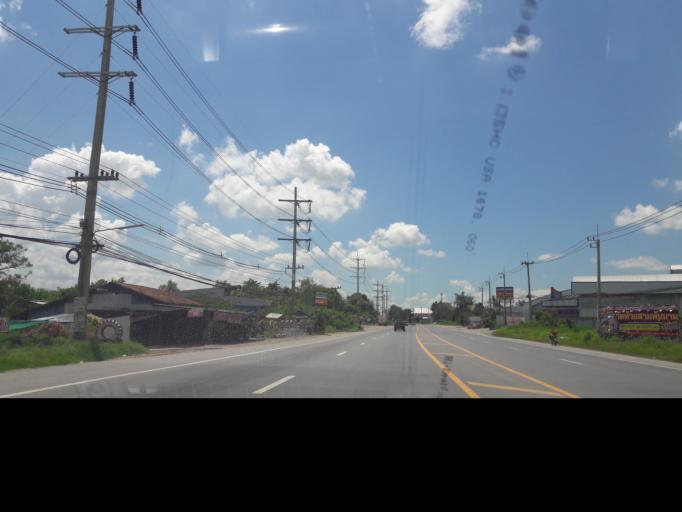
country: TH
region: Nakhon Pathom
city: Kamphaeng Saen
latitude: 14.0097
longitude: 100.0040
